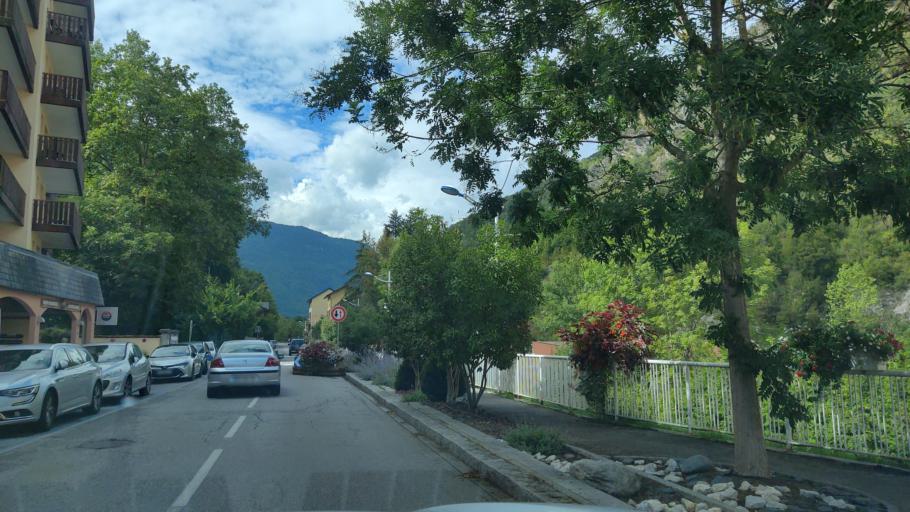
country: FR
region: Rhone-Alpes
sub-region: Departement de la Savoie
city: Les Allues
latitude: 45.4528
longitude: 6.5657
